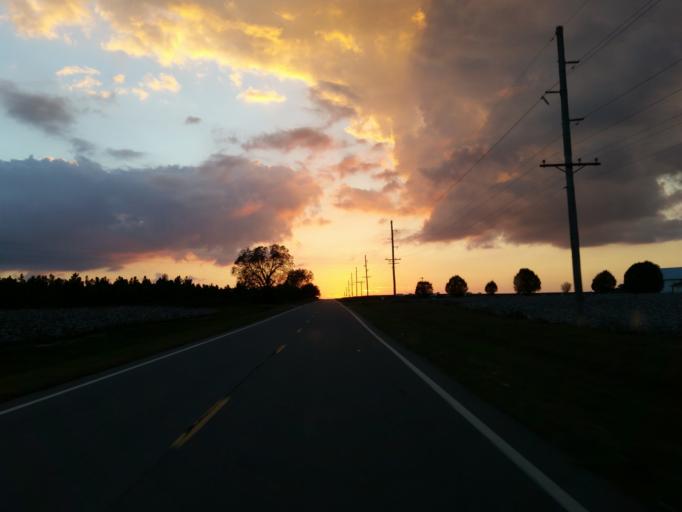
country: US
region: Georgia
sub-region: Dooly County
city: Unadilla
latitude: 32.1472
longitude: -83.6624
